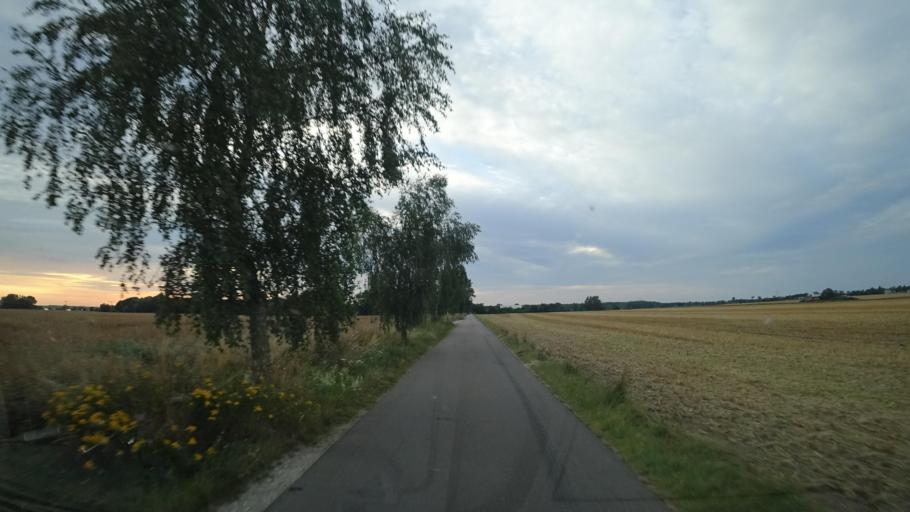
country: DE
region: Mecklenburg-Vorpommern
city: Kemnitz
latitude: 54.1005
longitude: 13.5166
